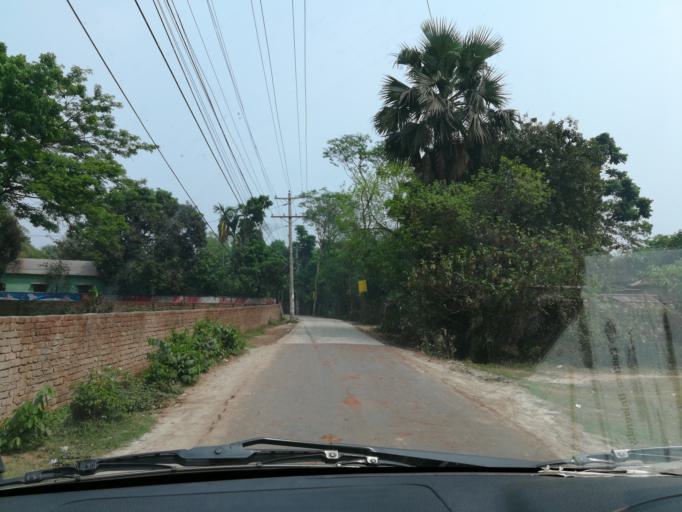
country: BD
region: Dhaka
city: Tungi
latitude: 23.8544
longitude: 90.3011
